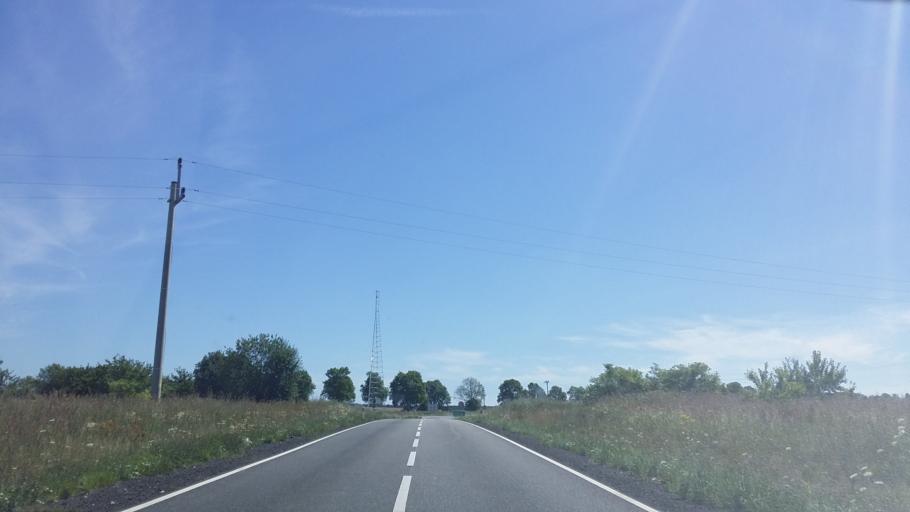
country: PL
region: West Pomeranian Voivodeship
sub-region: Powiat stargardzki
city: Insko
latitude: 53.4644
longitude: 15.5844
